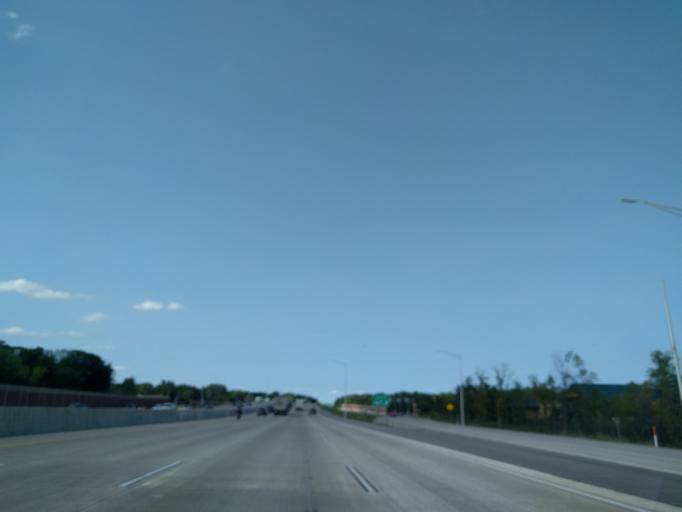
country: US
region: Wisconsin
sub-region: Brown County
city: Ashwaubenon
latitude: 44.5053
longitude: -88.0821
